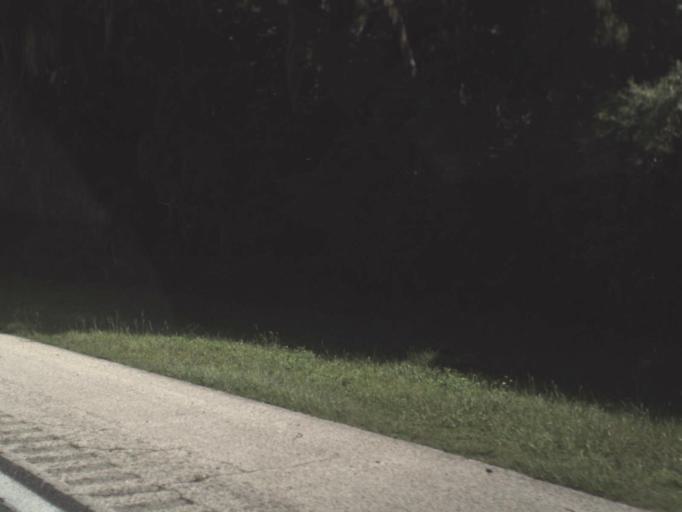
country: US
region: Florida
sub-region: Alachua County
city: Gainesville
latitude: 29.5525
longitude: -82.3399
